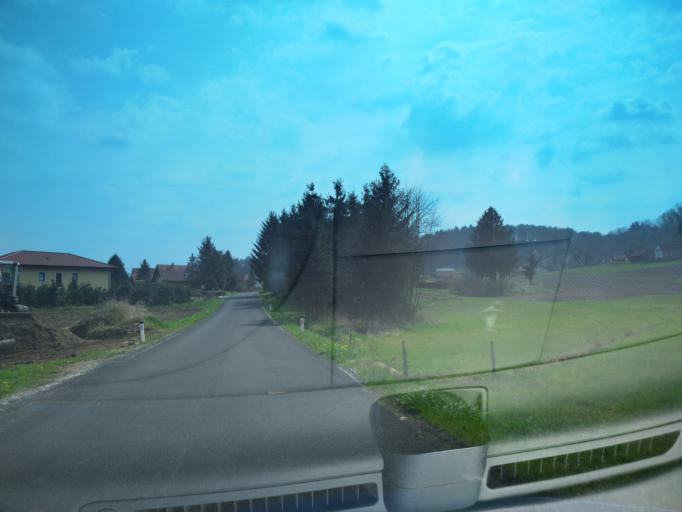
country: AT
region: Styria
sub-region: Politischer Bezirk Leibnitz
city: Kitzeck im Sausal
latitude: 46.7525
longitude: 15.4184
